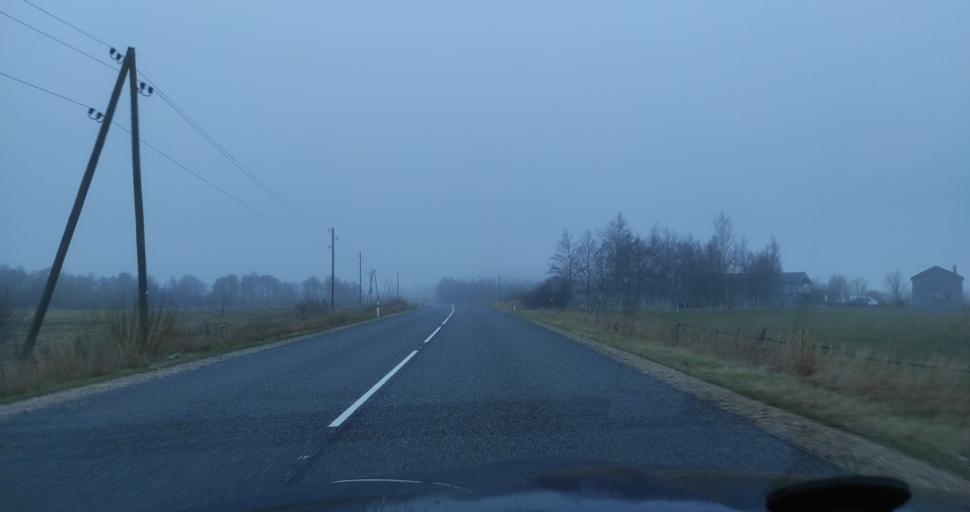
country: LV
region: Alsunga
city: Alsunga
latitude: 56.9901
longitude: 21.3636
